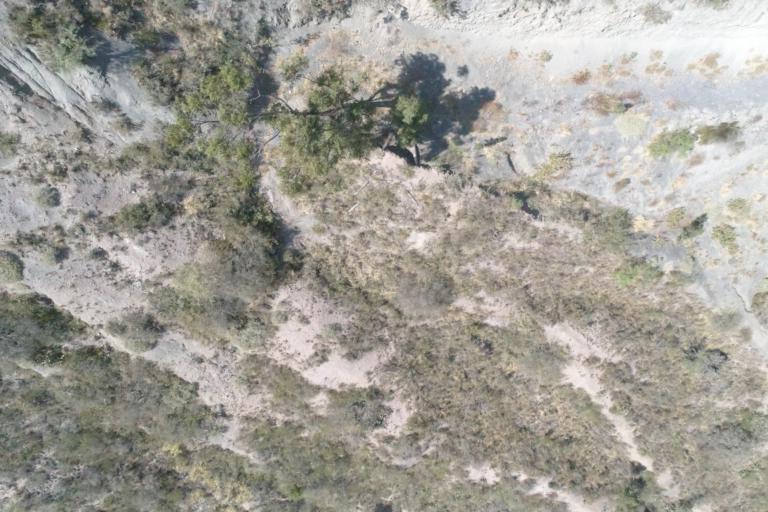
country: BO
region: La Paz
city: La Paz
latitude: -16.6214
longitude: -68.0397
